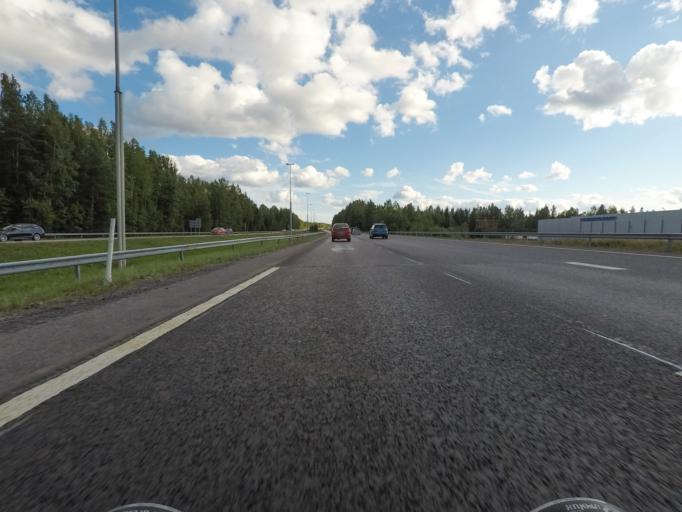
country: FI
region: Uusimaa
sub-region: Helsinki
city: Kerava
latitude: 60.3819
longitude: 25.1172
